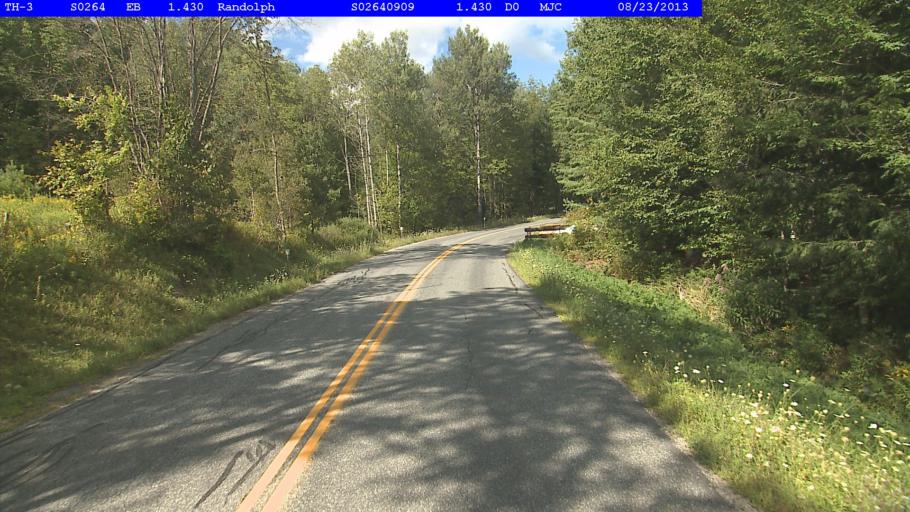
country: US
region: Vermont
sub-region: Orange County
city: Chelsea
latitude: 43.9489
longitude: -72.5376
